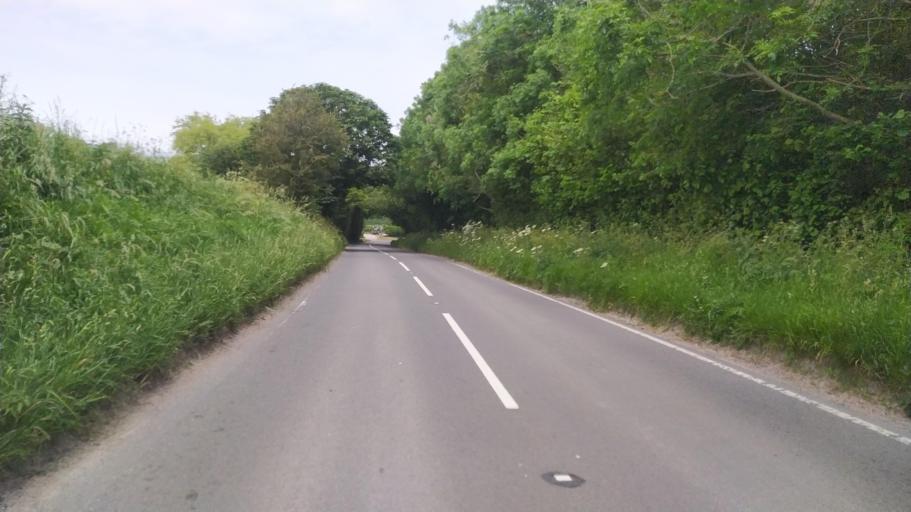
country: GB
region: England
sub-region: Dorset
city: Dorchester
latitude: 50.8022
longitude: -2.4799
